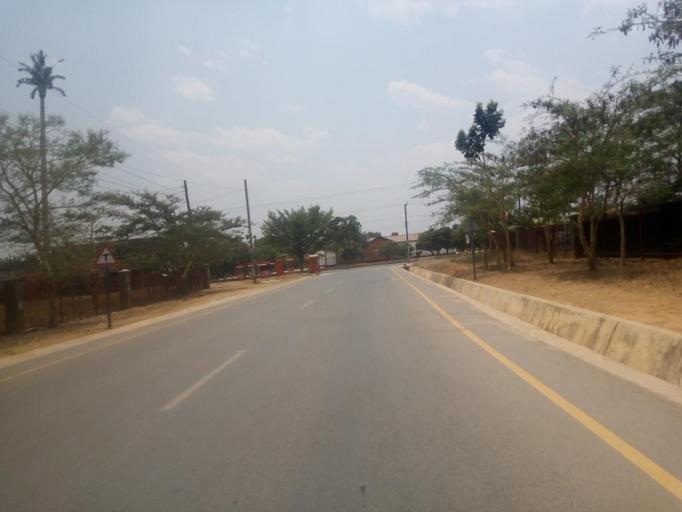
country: ZM
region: Lusaka
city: Lusaka
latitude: -15.3939
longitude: 28.3941
